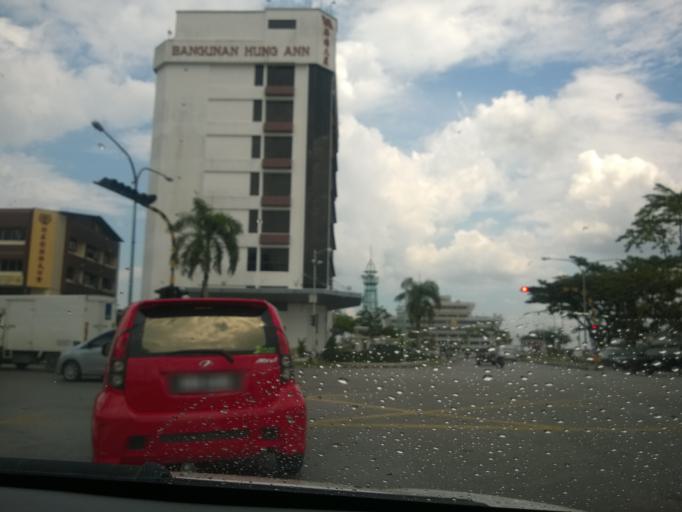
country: MY
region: Sarawak
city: Sibu
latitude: 2.2928
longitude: 111.8245
